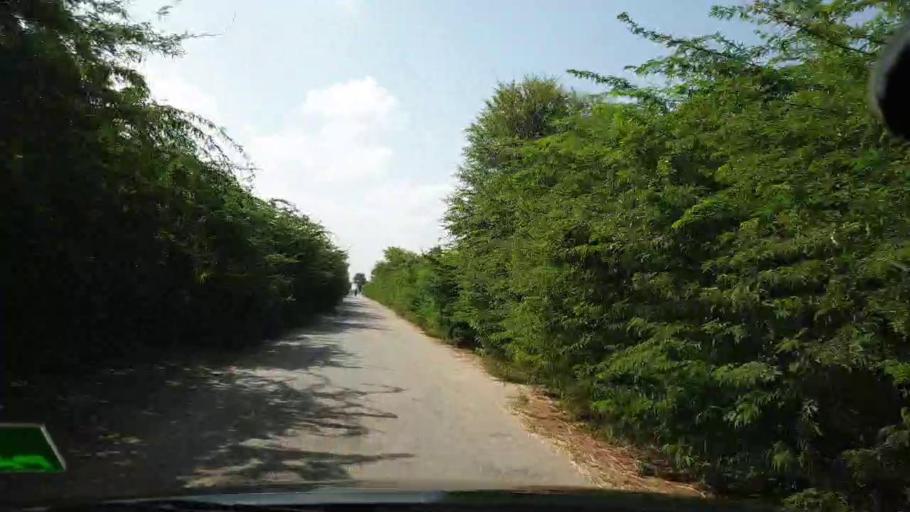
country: PK
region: Sindh
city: Kadhan
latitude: 24.6361
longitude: 69.1158
